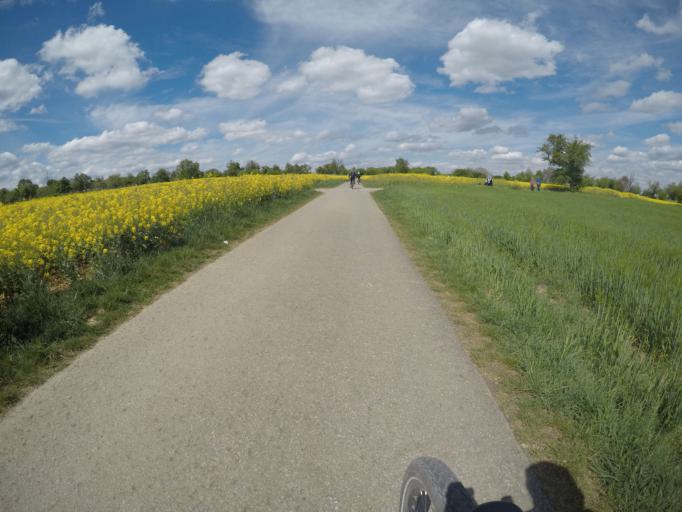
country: DE
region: Baden-Wuerttemberg
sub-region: Regierungsbezirk Stuttgart
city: Gartringen
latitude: 48.6404
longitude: 8.8806
